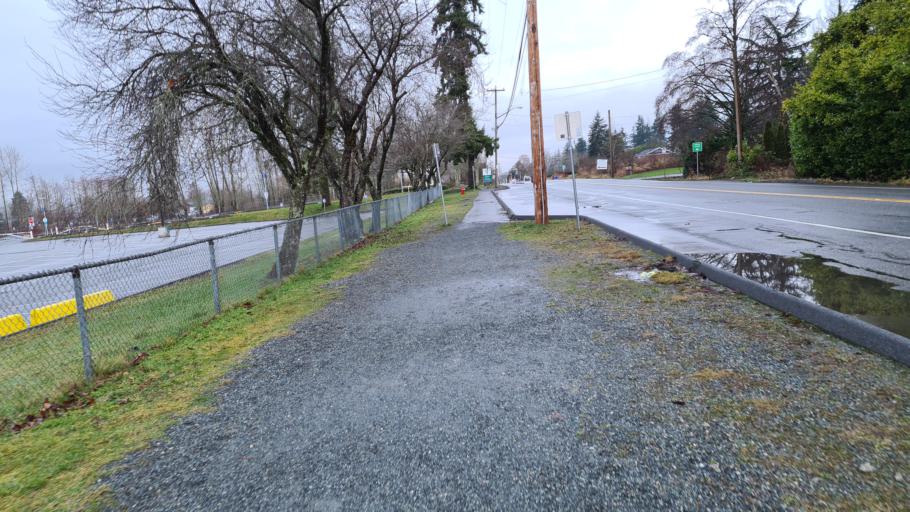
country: CA
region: British Columbia
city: Walnut Grove
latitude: 49.1446
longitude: -122.6616
